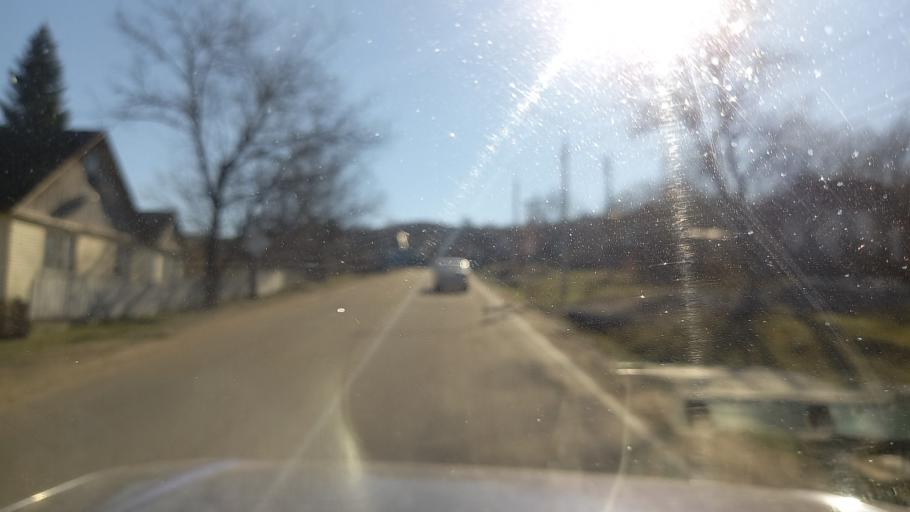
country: RU
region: Adygeya
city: Kamennomostskiy
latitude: 44.2877
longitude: 40.2035
